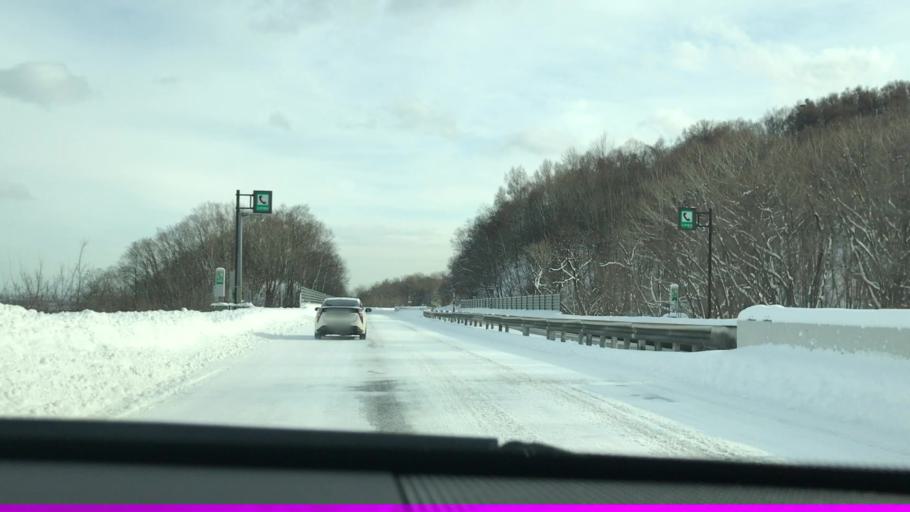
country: JP
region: Hokkaido
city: Otaru
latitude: 43.1459
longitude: 141.1362
